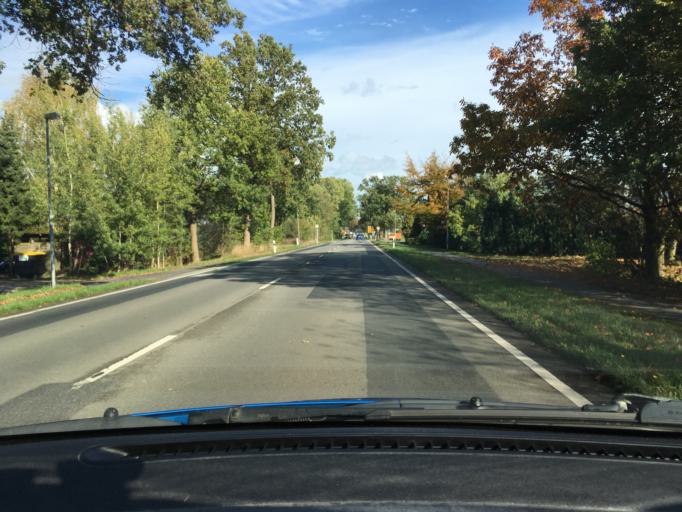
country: DE
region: Lower Saxony
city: Wistedt
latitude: 53.2675
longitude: 9.6765
